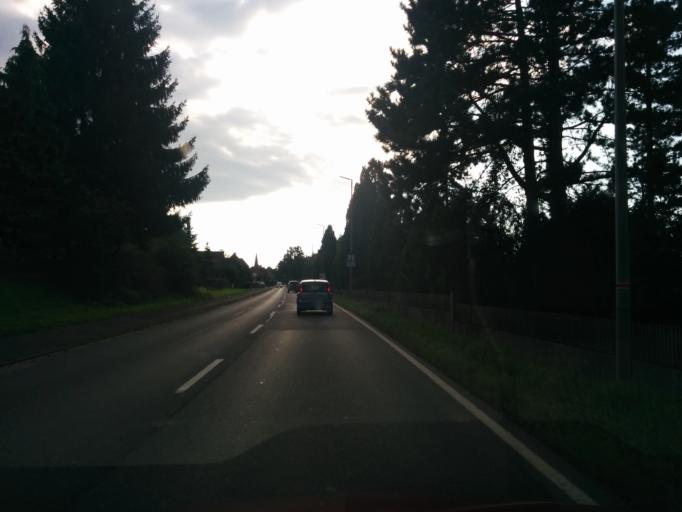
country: DE
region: Lower Saxony
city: Northeim
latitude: 51.7080
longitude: 10.0165
